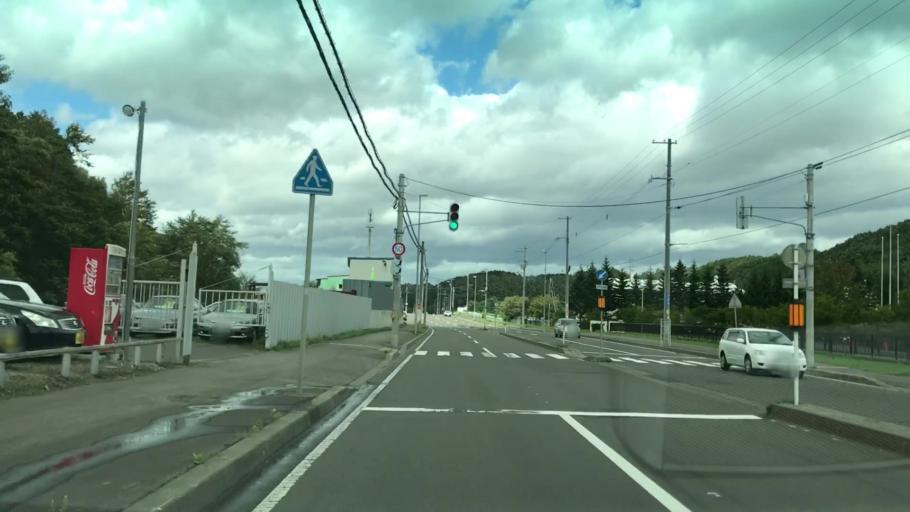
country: JP
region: Hokkaido
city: Kitahiroshima
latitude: 42.9715
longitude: 141.4516
